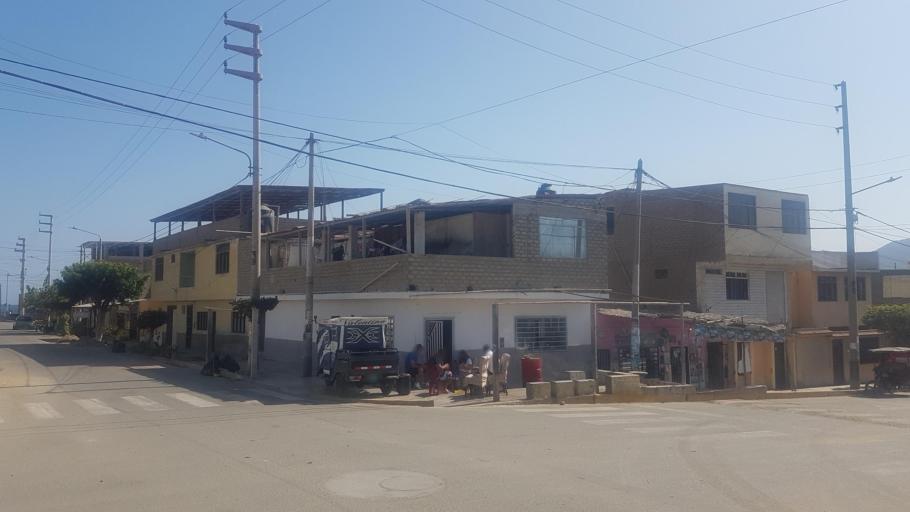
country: PE
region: Ancash
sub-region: Provincia de Santa
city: Chimbote
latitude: -9.0937
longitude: -78.5725
